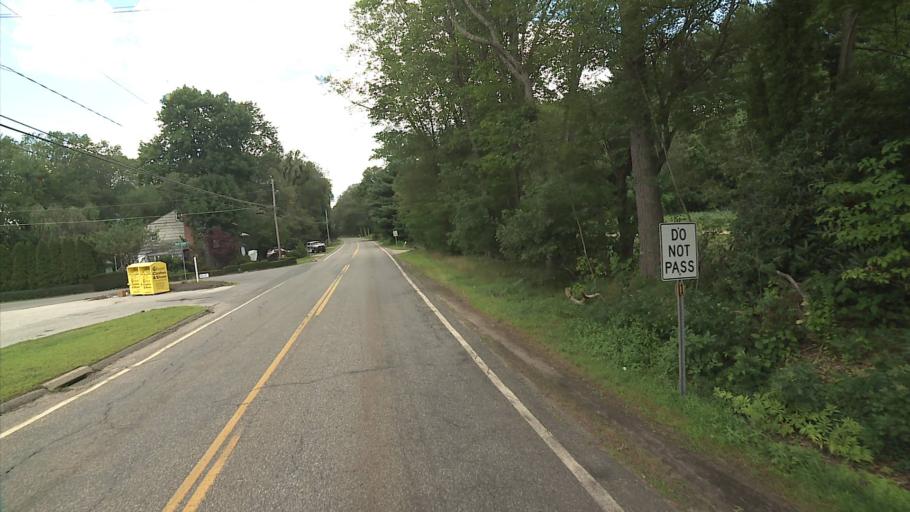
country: US
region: Connecticut
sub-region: Tolland County
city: Stafford
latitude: 41.9349
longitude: -72.1929
